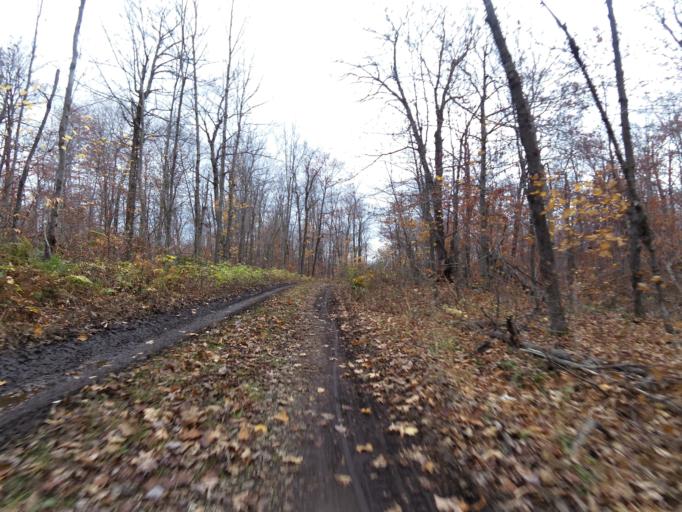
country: CA
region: Quebec
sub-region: Outaouais
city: Wakefield
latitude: 45.5548
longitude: -75.9774
